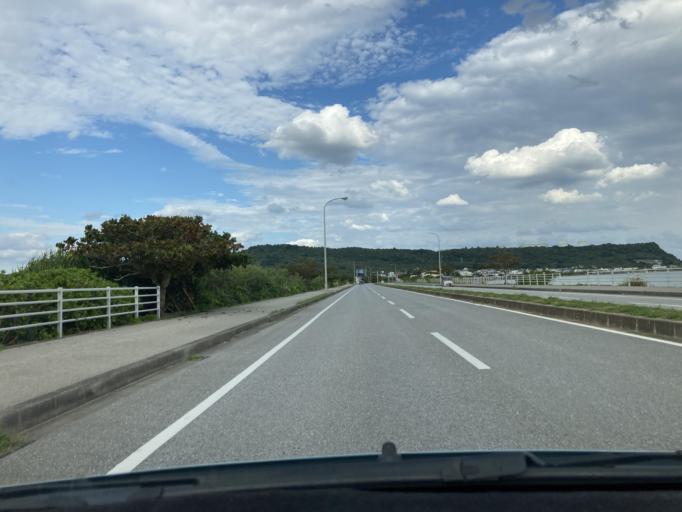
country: JP
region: Okinawa
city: Katsuren-haebaru
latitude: 26.3370
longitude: 127.9411
